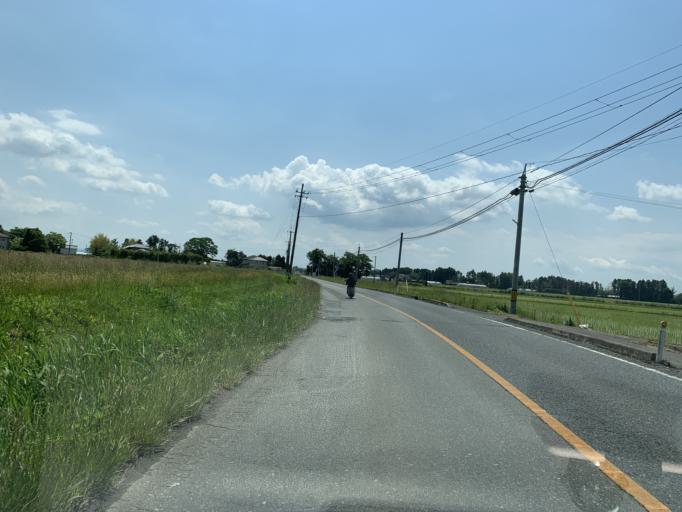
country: JP
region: Miyagi
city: Kogota
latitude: 38.5707
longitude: 141.0392
